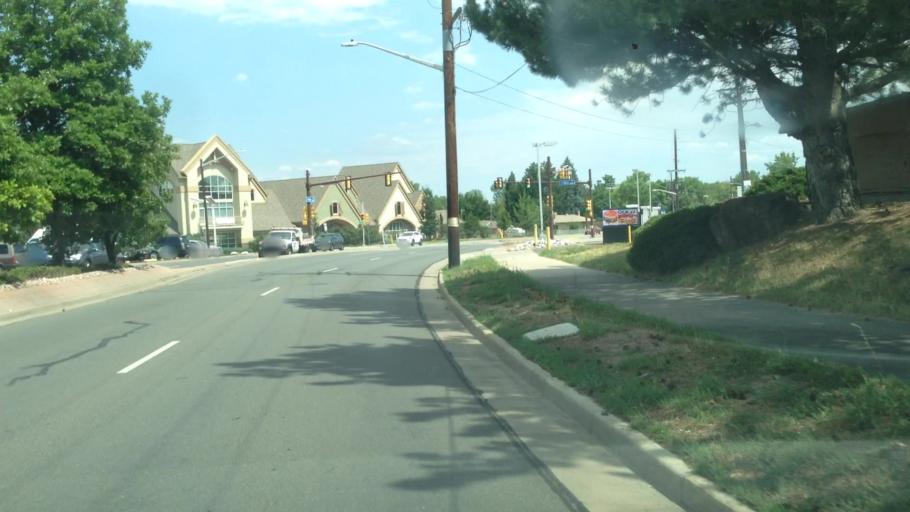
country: US
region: Colorado
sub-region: Jefferson County
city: Arvada
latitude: 39.8126
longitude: -105.1156
